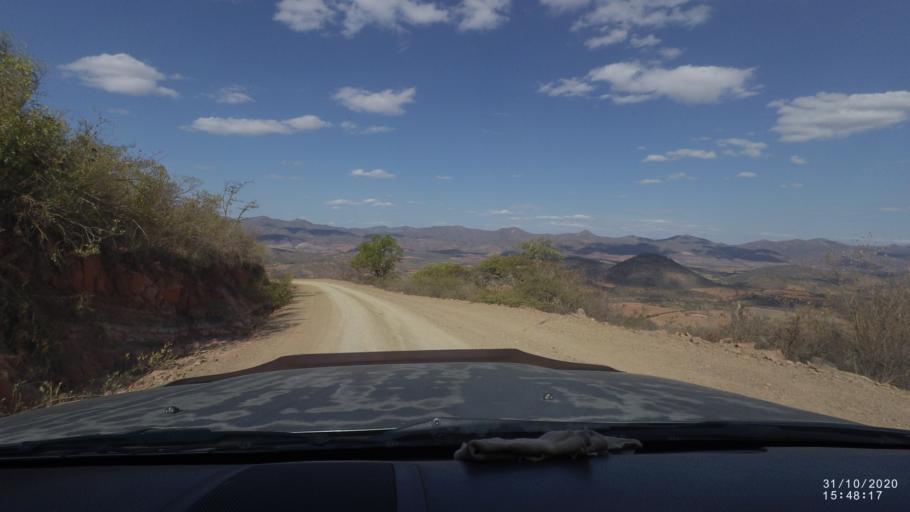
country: BO
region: Chuquisaca
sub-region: Provincia Zudanez
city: Mojocoya
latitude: -18.3129
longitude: -64.7109
